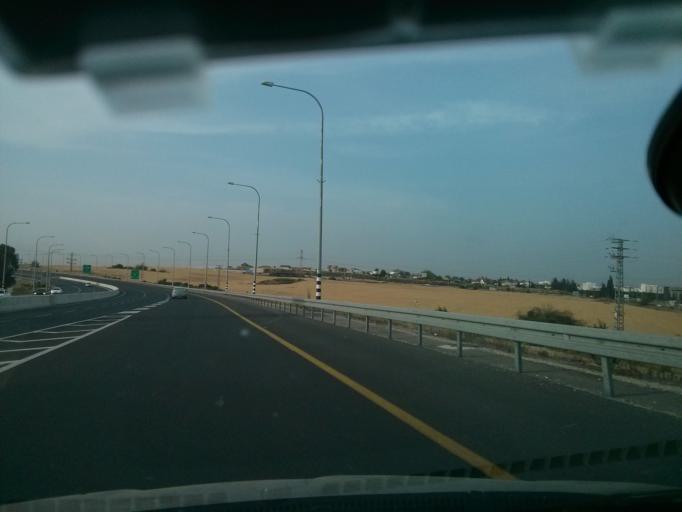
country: IL
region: Central District
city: Gedera
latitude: 31.8007
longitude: 34.7638
